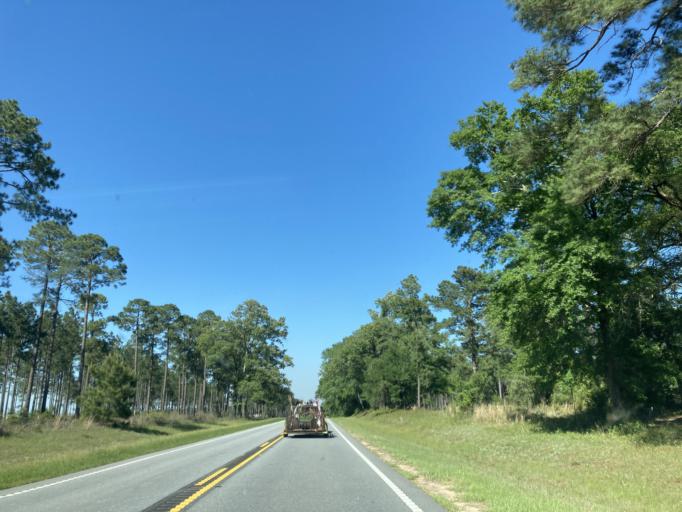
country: US
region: Georgia
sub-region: Baker County
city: Newton
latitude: 31.3588
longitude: -84.2959
